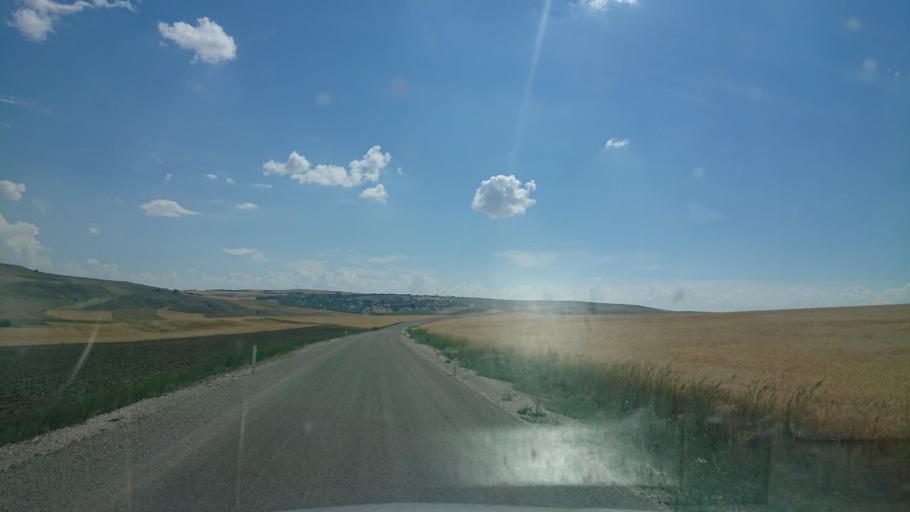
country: TR
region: Aksaray
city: Agacoren
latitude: 38.7867
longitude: 33.8095
